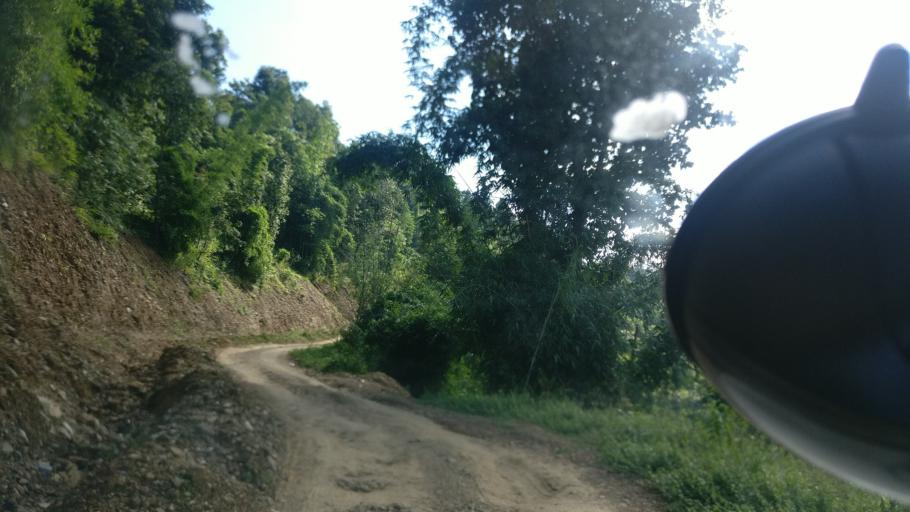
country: NP
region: Western Region
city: Baglung
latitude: 28.1389
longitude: 83.6499
